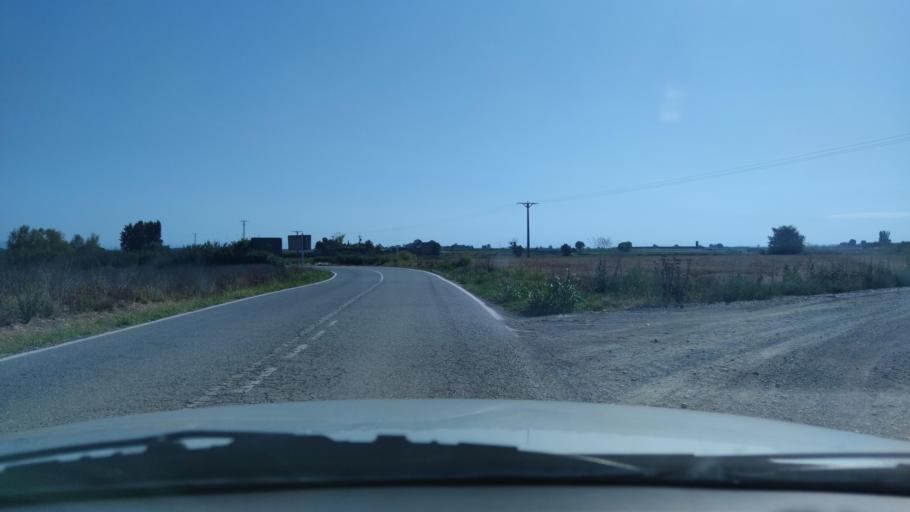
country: ES
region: Catalonia
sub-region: Provincia de Lleida
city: Sidamon
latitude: 41.6385
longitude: 0.7920
